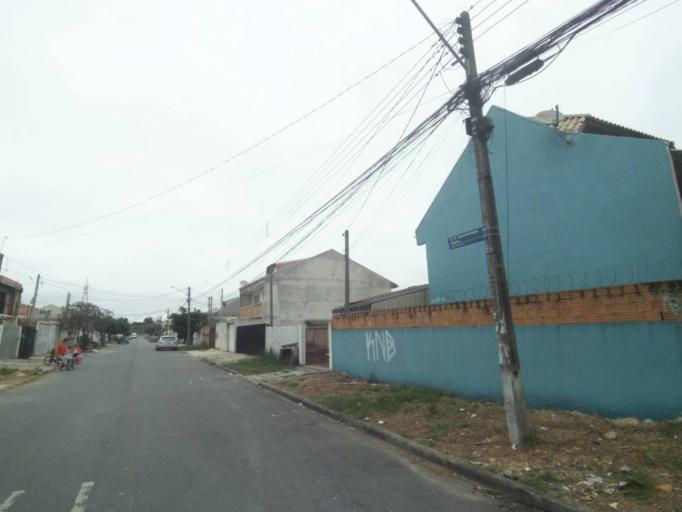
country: BR
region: Parana
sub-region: Araucaria
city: Araucaria
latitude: -25.5503
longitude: -49.3384
